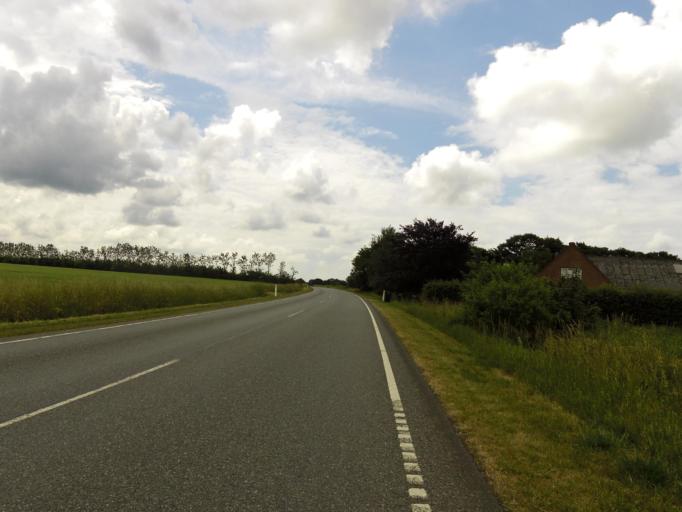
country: DK
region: South Denmark
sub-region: Tonder Kommune
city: Sherrebek
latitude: 55.2169
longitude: 8.8943
